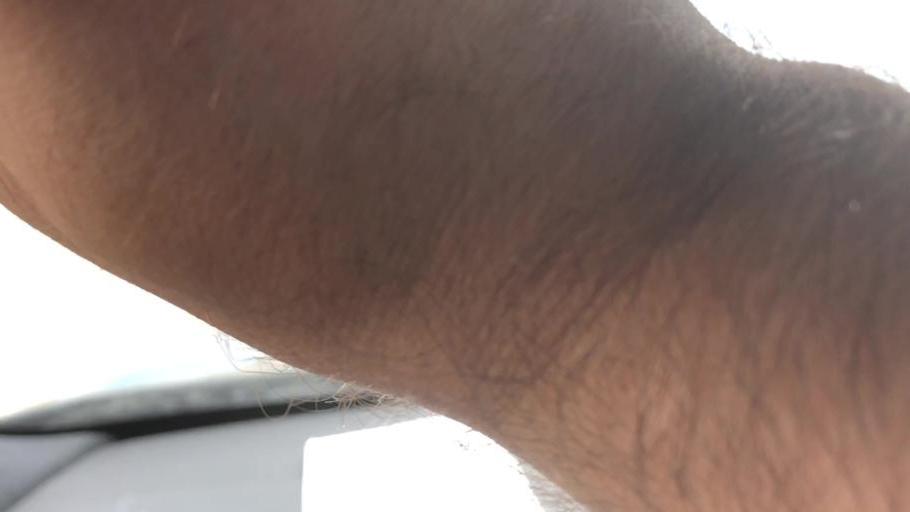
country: US
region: California
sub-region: Riverside County
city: Mesa Verde
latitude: 33.6068
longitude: -114.7134
